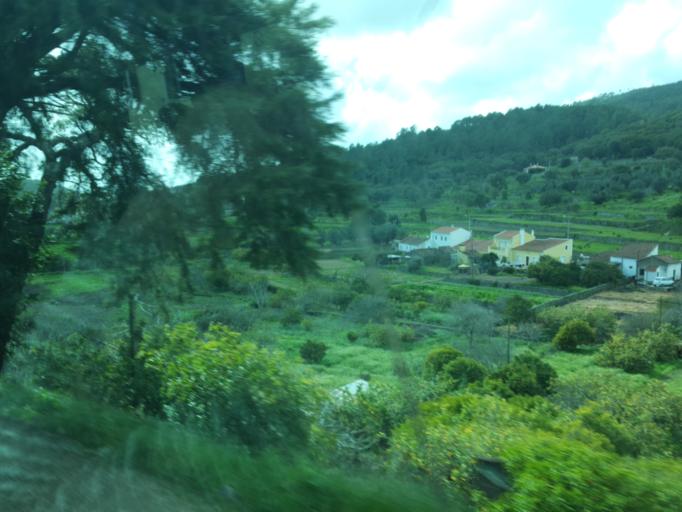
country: PT
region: Faro
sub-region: Monchique
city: Monchique
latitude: 37.3027
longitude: -8.5624
